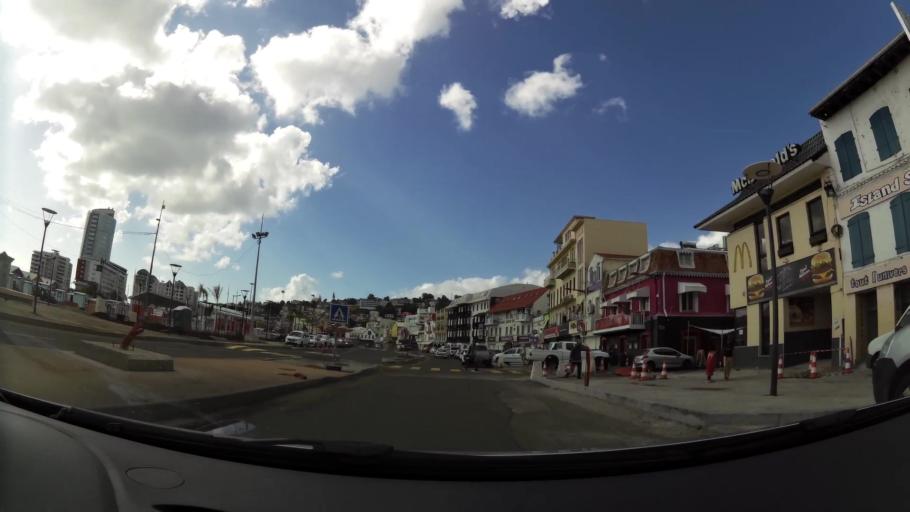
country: MQ
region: Martinique
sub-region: Martinique
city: Fort-de-France
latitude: 14.6031
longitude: -61.0700
